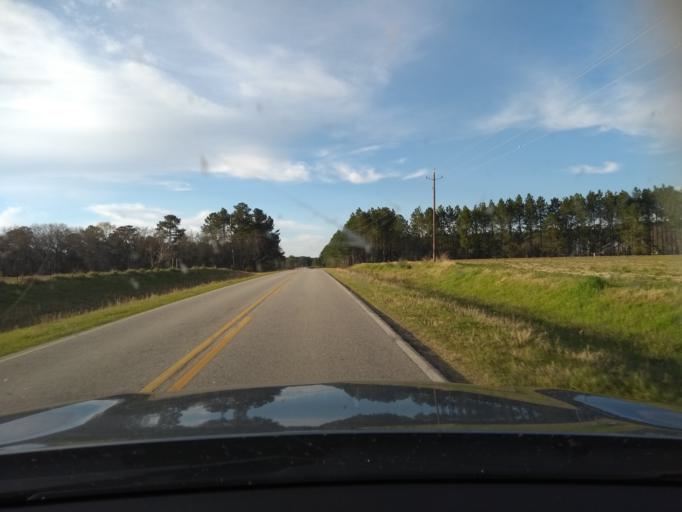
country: US
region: Georgia
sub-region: Bulloch County
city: Brooklet
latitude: 32.3094
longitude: -81.7754
